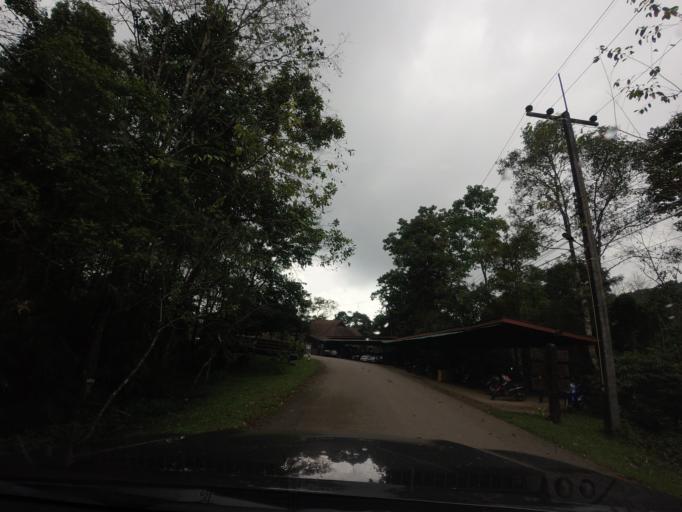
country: TH
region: Nan
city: Bo Kluea
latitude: 19.2011
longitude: 101.0810
